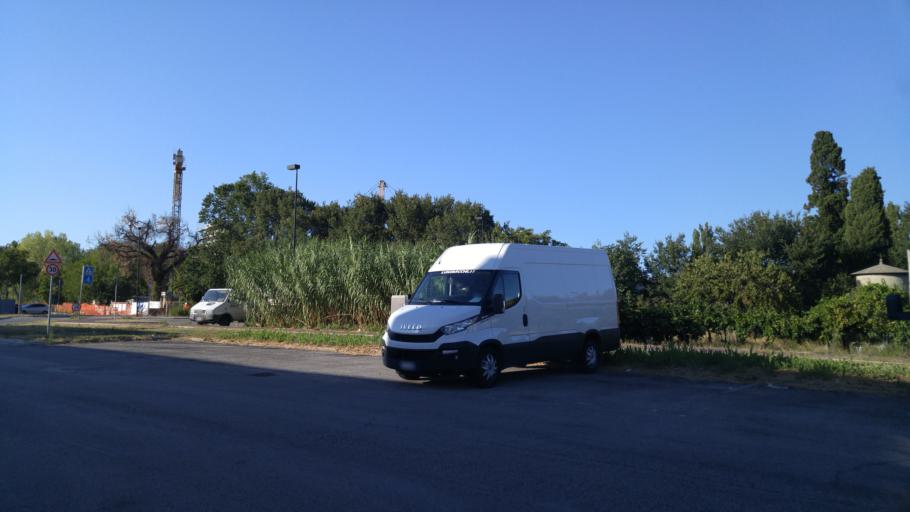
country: IT
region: The Marches
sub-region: Provincia di Pesaro e Urbino
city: Pesaro
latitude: 43.8871
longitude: 12.8778
